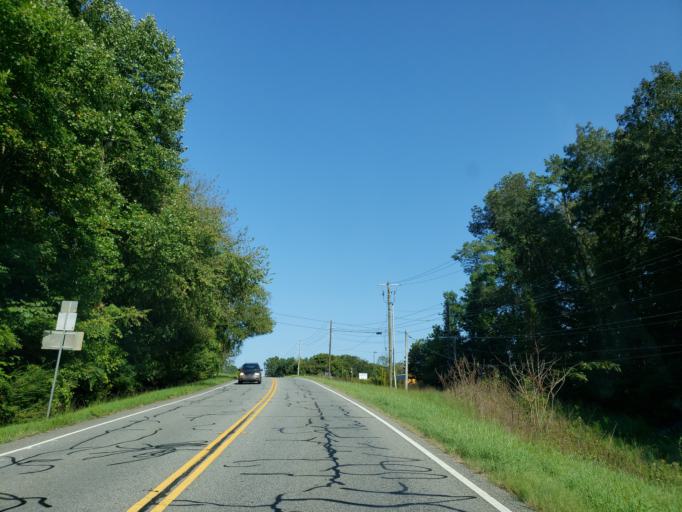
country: US
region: Georgia
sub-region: Catoosa County
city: Ringgold
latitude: 34.9052
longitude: -85.0741
